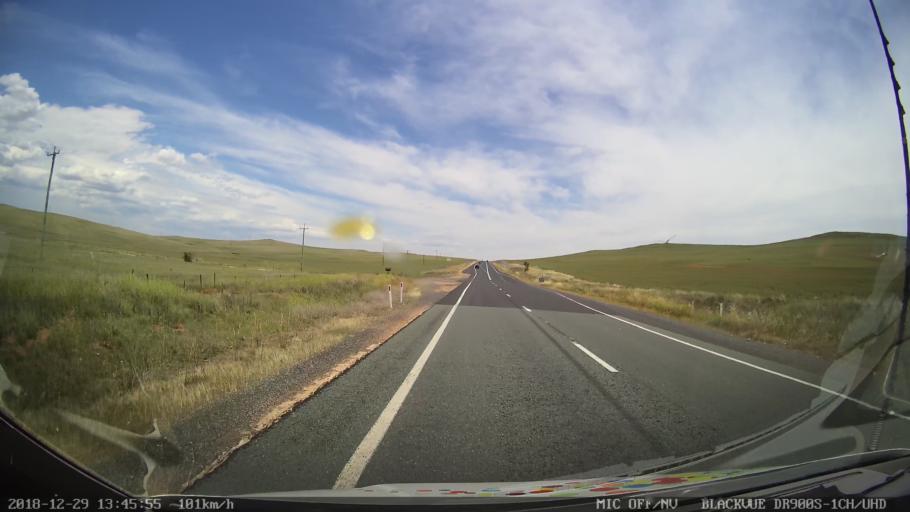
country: AU
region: New South Wales
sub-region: Cooma-Monaro
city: Cooma
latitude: -36.1039
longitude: 149.1446
